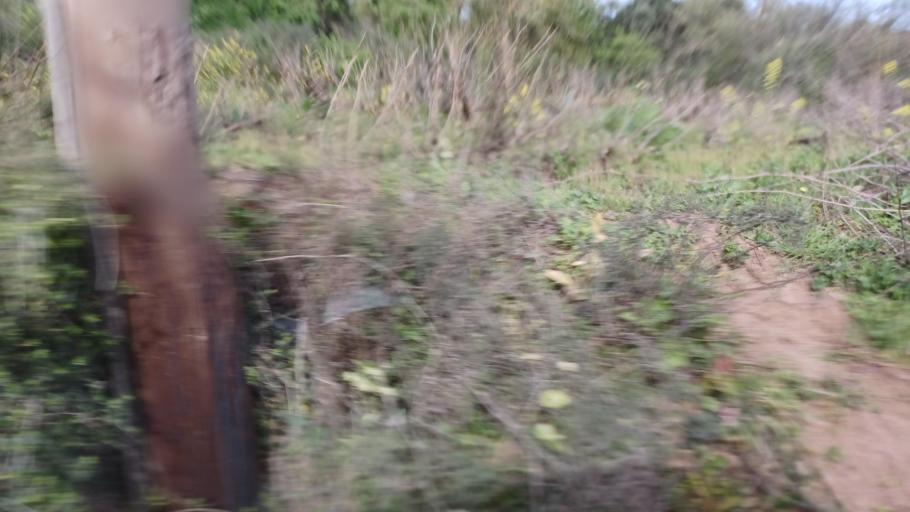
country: CY
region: Pafos
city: Pegeia
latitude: 34.9625
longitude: 32.3803
